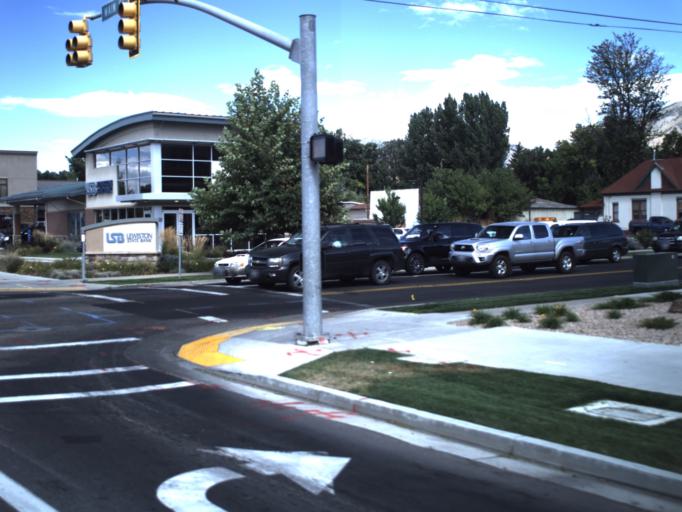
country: US
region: Utah
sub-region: Cache County
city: Logan
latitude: 41.7257
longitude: -111.8351
